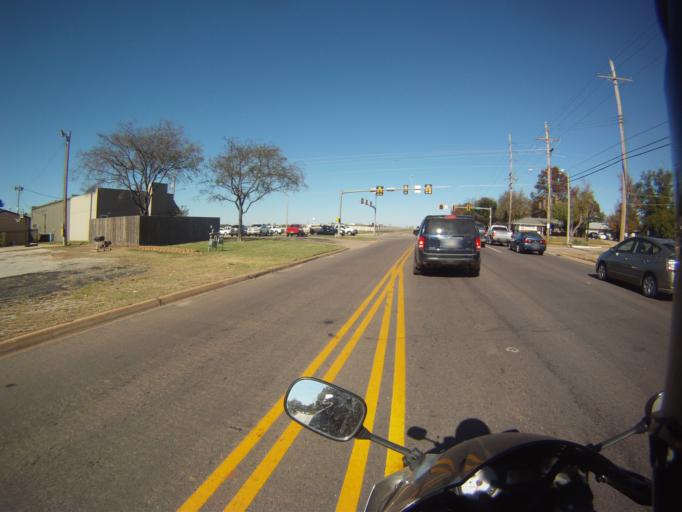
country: US
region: Oklahoma
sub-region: Payne County
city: Stillwater
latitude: 36.1153
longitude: -97.0874
